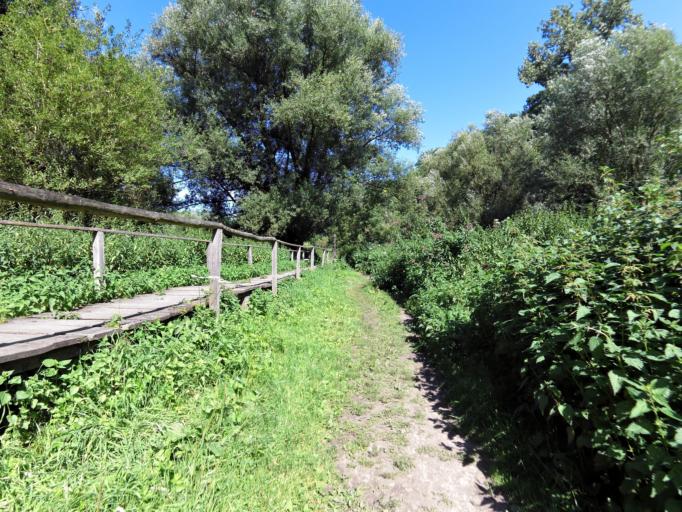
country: DE
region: North Rhine-Westphalia
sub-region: Regierungsbezirk Koln
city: Herzogenrath
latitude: 50.8503
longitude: 6.0888
